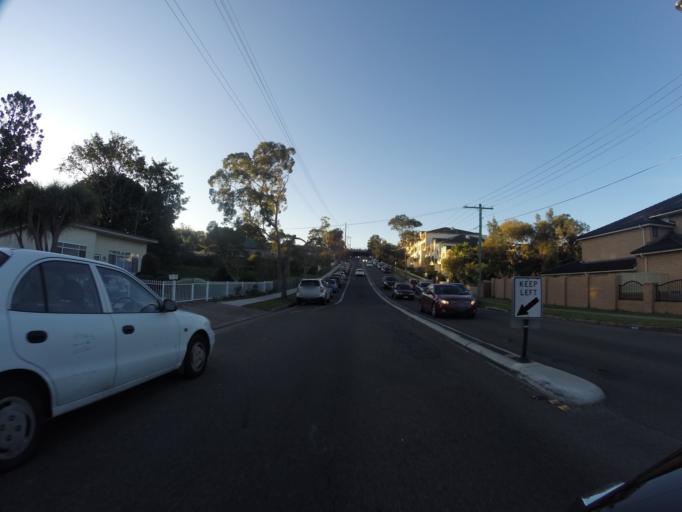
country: AU
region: New South Wales
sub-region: Sutherland Shire
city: Miranda
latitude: -34.0379
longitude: 151.0978
